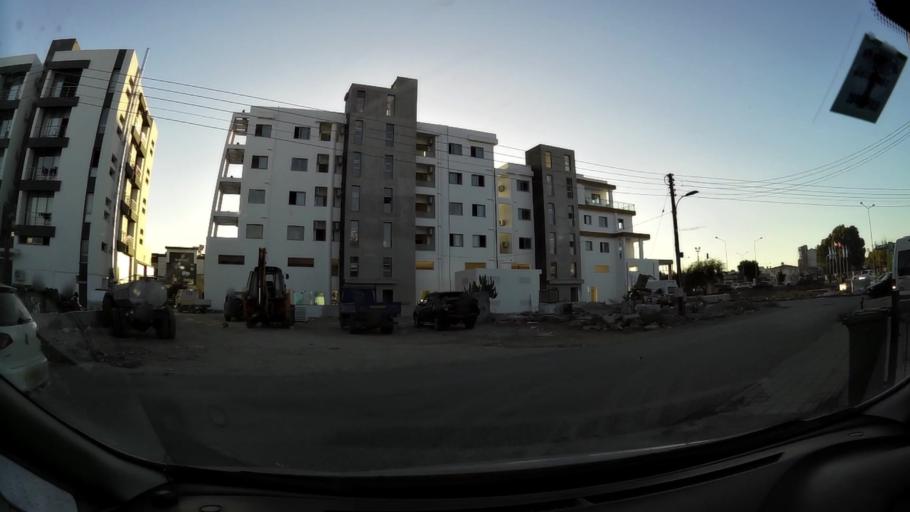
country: CY
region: Lefkosia
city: Nicosia
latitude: 35.2076
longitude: 33.3162
